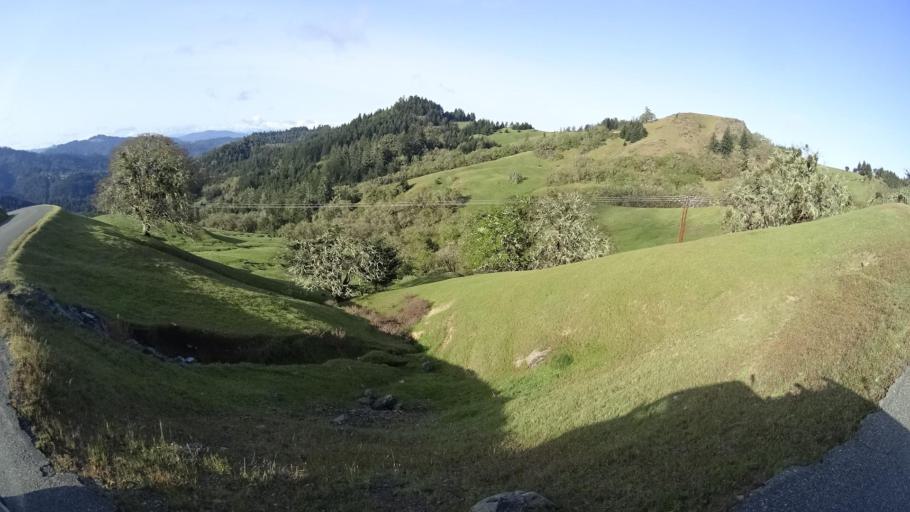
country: US
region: California
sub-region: Humboldt County
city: Blue Lake
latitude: 40.7188
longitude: -123.9423
